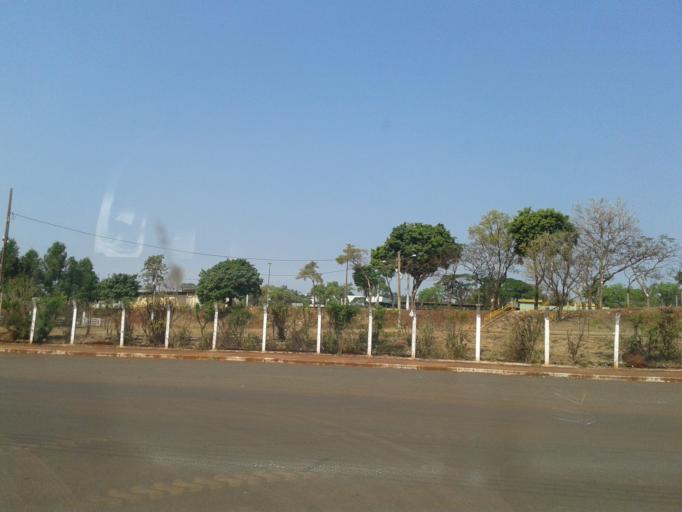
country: BR
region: Minas Gerais
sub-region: Ituiutaba
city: Ituiutaba
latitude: -18.9707
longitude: -49.4846
